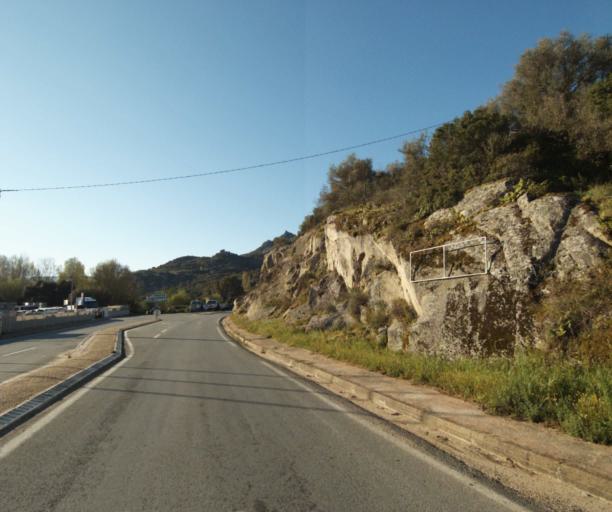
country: FR
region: Corsica
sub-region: Departement de la Corse-du-Sud
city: Propriano
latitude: 41.6563
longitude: 8.9177
